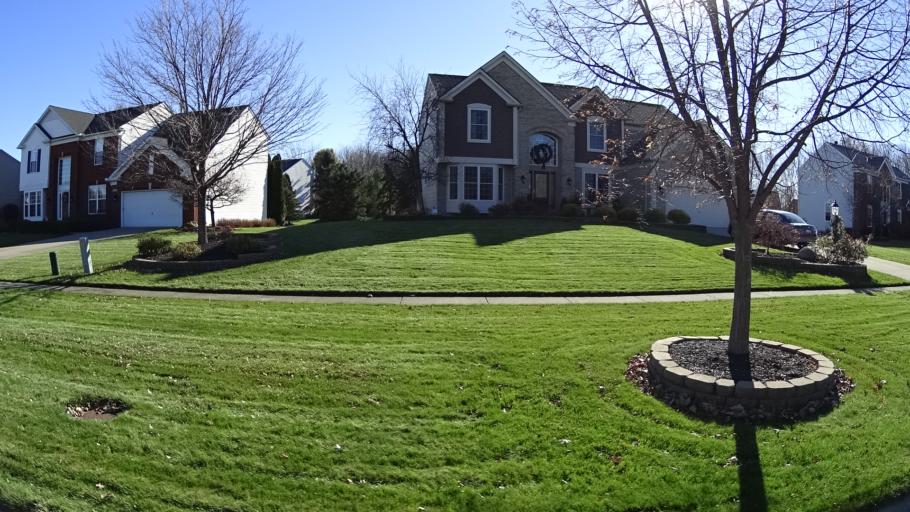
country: US
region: Ohio
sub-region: Lorain County
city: Avon
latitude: 41.4301
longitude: -82.0250
